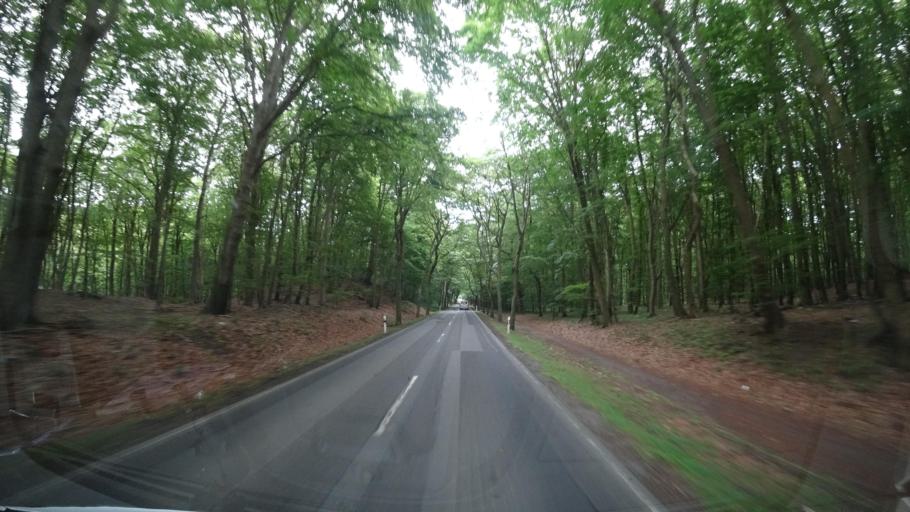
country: DE
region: Mecklenburg-Vorpommern
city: Putbus
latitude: 54.3483
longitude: 13.4451
